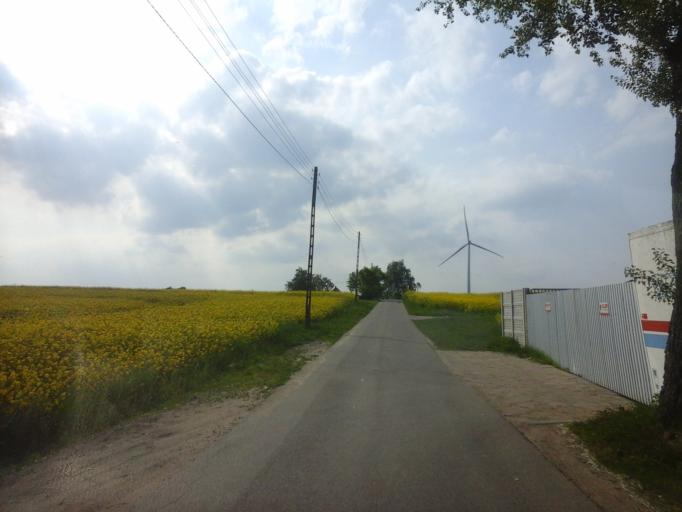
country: PL
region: West Pomeranian Voivodeship
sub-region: Powiat choszczenski
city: Pelczyce
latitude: 53.0316
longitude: 15.2711
